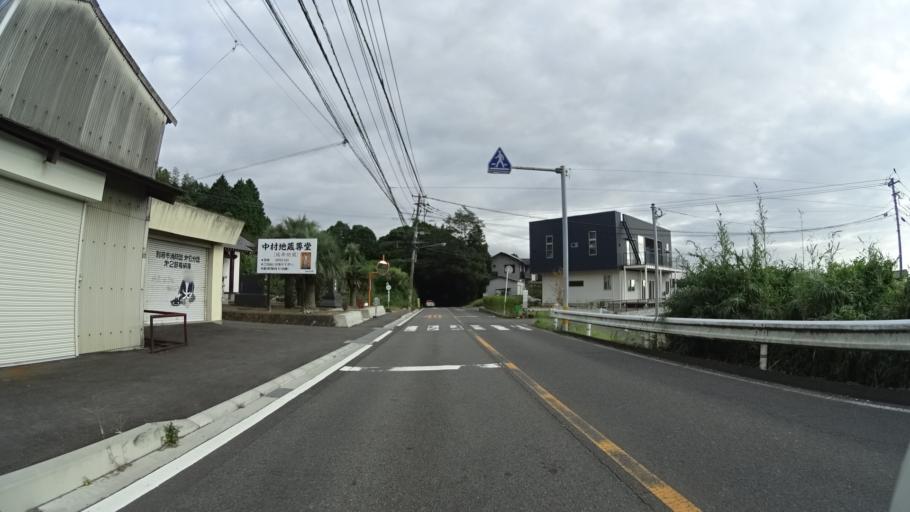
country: JP
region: Oita
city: Beppu
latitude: 33.3234
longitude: 131.4785
